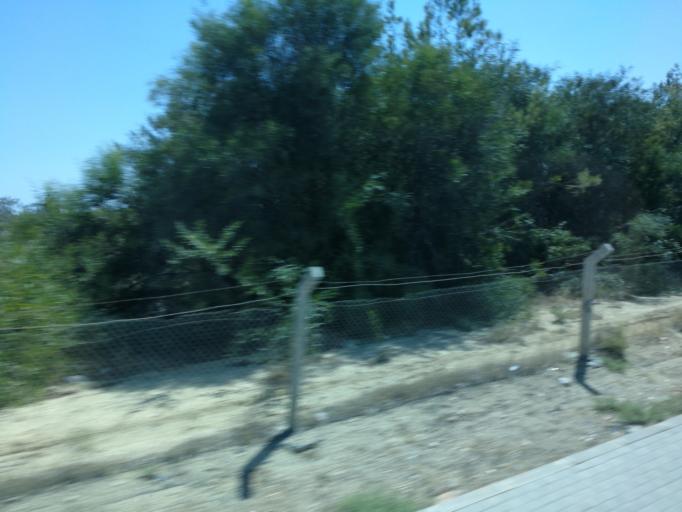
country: CY
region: Ammochostos
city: Famagusta
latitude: 35.1536
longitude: 33.9058
